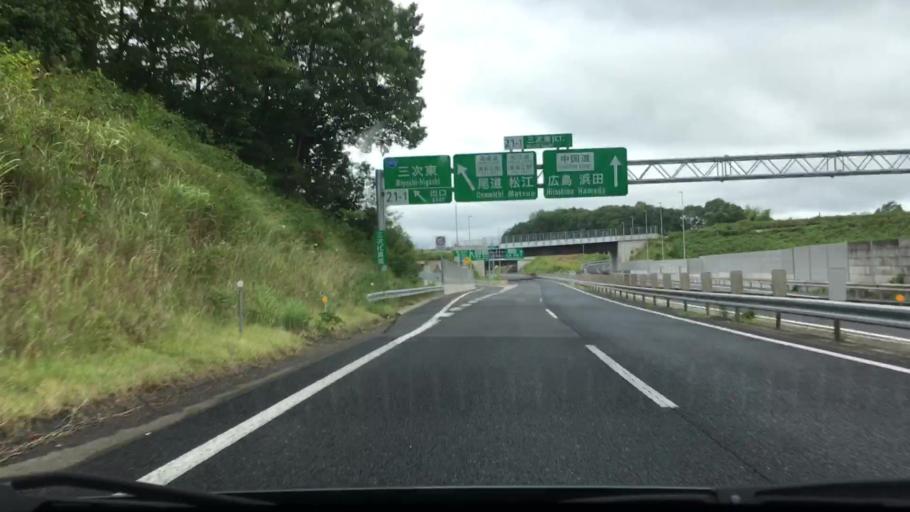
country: JP
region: Hiroshima
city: Miyoshi
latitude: 34.8029
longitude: 132.9132
